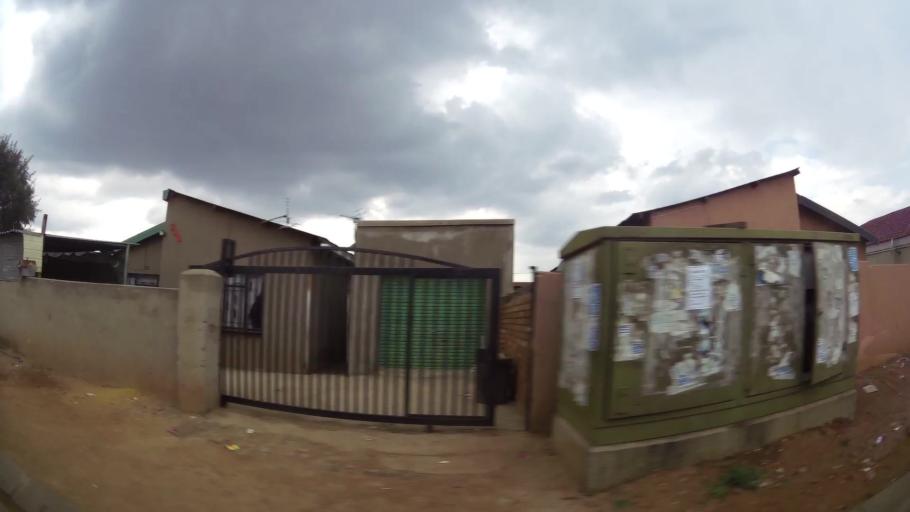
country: ZA
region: Gauteng
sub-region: Ekurhuleni Metropolitan Municipality
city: Germiston
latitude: -26.3642
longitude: 28.1614
